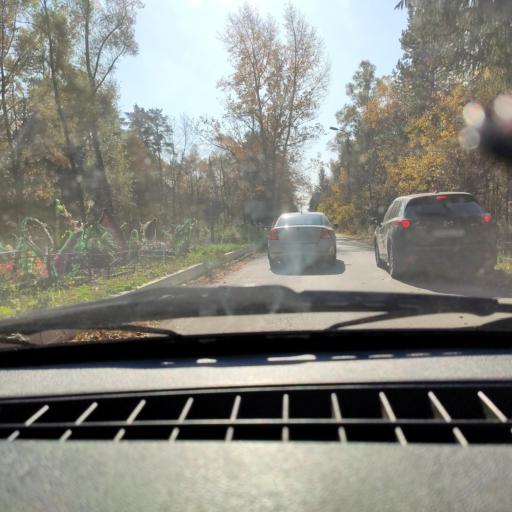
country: RU
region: Bashkortostan
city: Mikhaylovka
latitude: 54.8110
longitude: 55.8630
